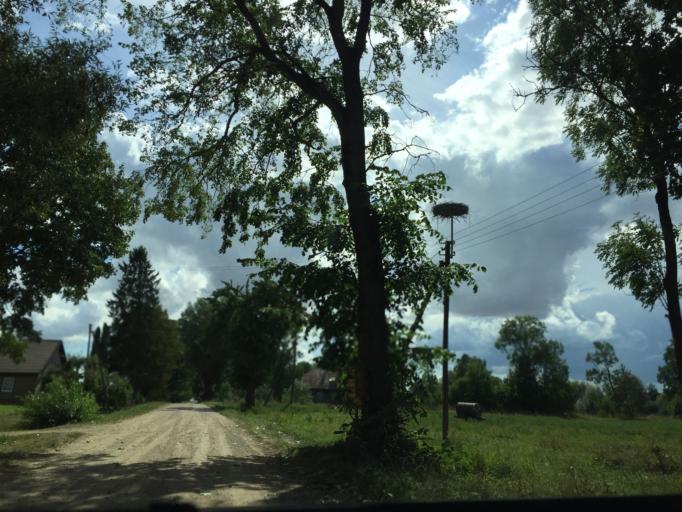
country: LT
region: Siauliu apskritis
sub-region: Joniskis
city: Joniskis
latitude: 56.3464
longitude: 23.6235
